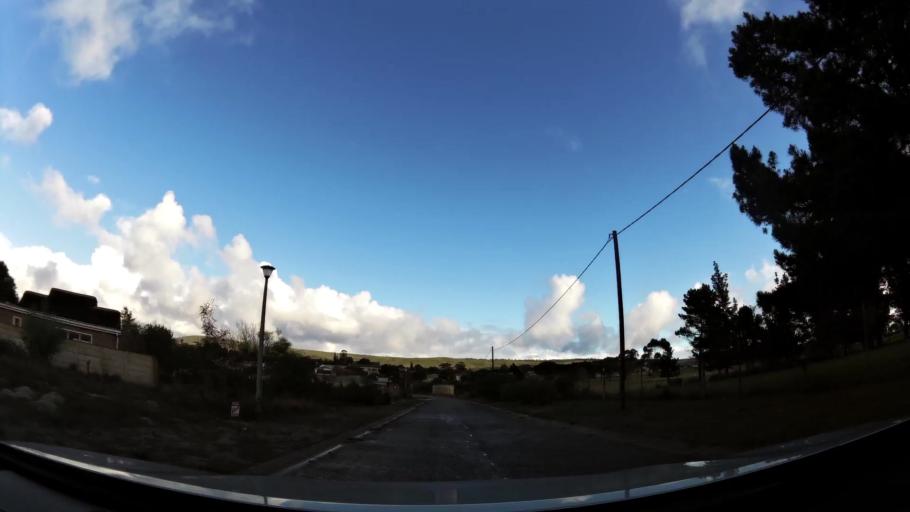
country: ZA
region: Western Cape
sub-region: Eden District Municipality
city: Riversdale
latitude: -34.2003
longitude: 21.5819
